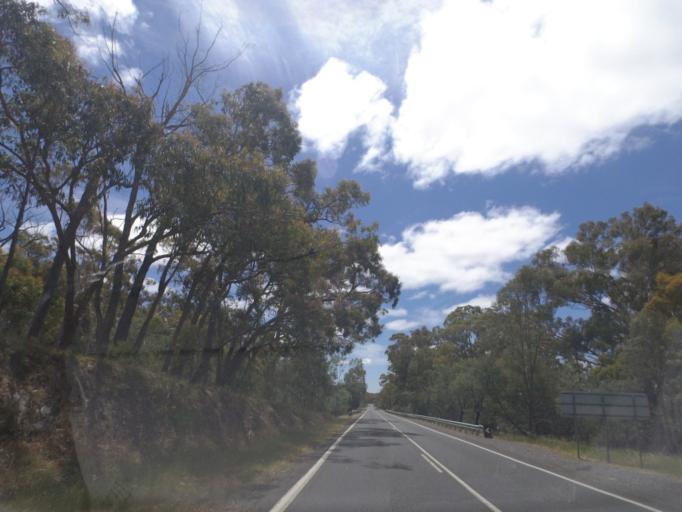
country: AU
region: Victoria
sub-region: Mount Alexander
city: Castlemaine
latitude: -37.2983
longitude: 144.1624
